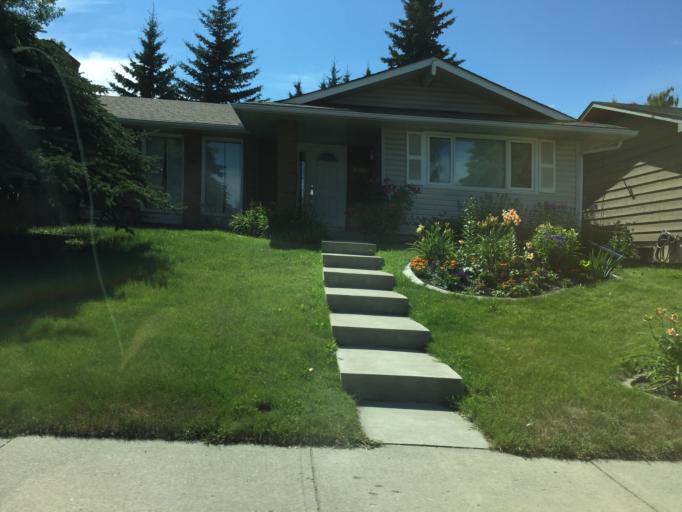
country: CA
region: Alberta
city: Calgary
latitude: 50.9311
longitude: -114.0388
